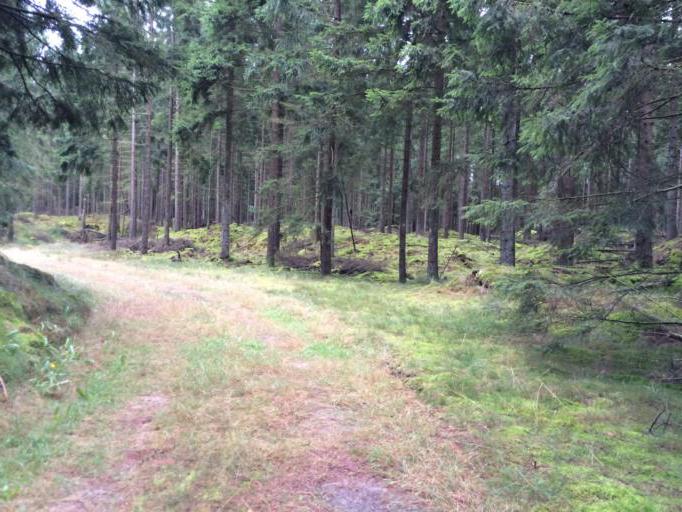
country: DK
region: Central Jutland
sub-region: Holstebro Kommune
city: Ulfborg
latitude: 56.2304
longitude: 8.4202
